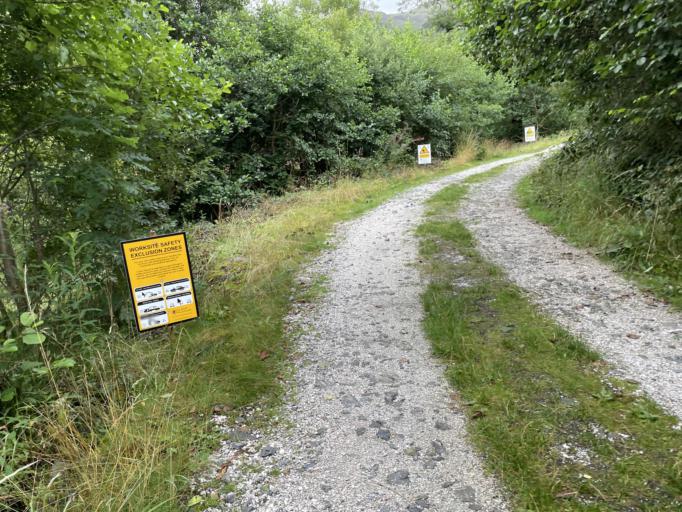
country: GB
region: Scotland
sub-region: Dumfries and Galloway
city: Newton Stewart
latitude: 55.0890
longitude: -4.4580
